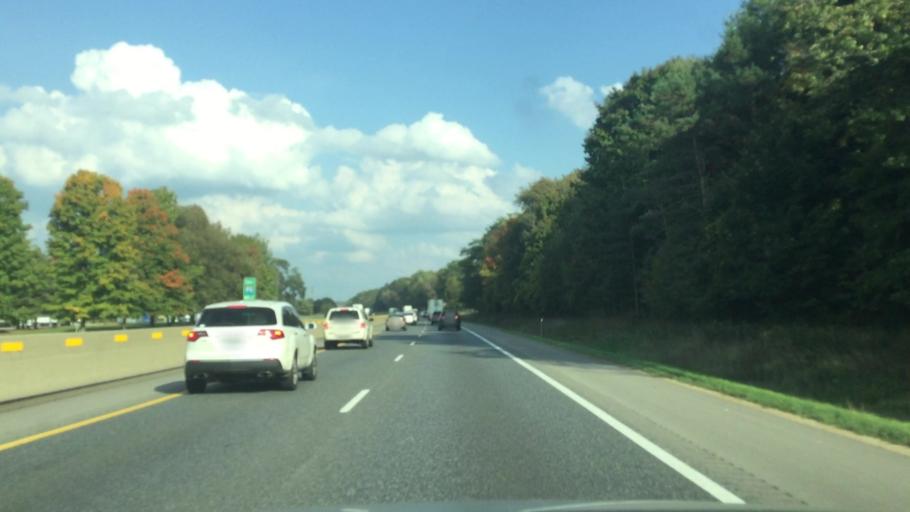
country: US
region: Michigan
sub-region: Kalamazoo County
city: Galesburg
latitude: 42.2698
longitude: -85.4462
